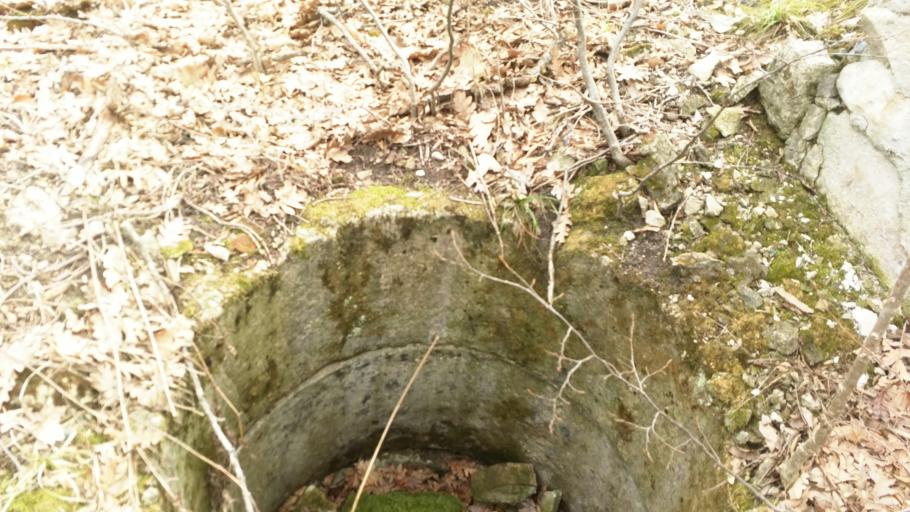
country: RU
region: Stavropol'skiy
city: Zheleznovodsk
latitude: 44.1270
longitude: 43.0223
